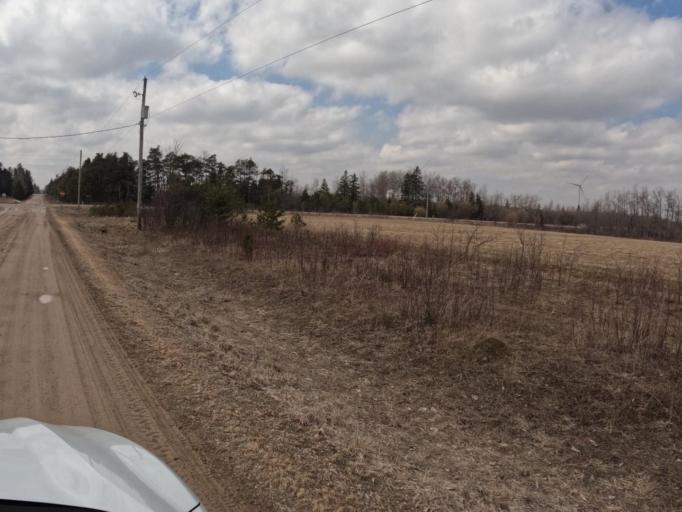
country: CA
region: Ontario
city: Shelburne
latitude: 44.0248
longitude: -80.2778
